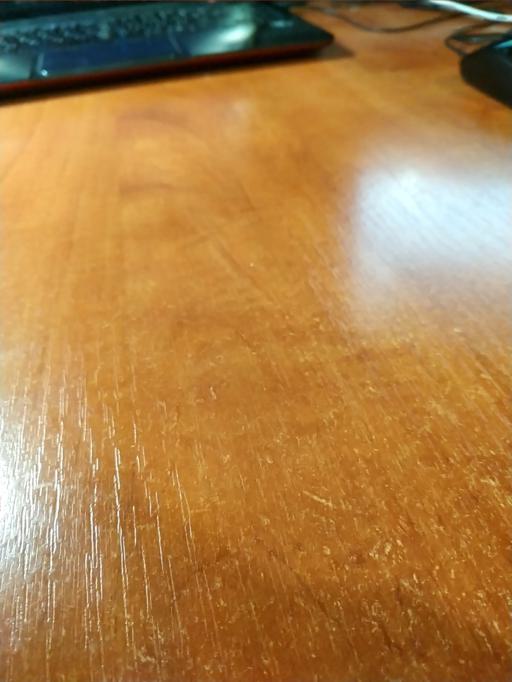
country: RU
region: Tverskaya
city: Vyshniy Volochek
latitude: 57.3546
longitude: 34.5815
